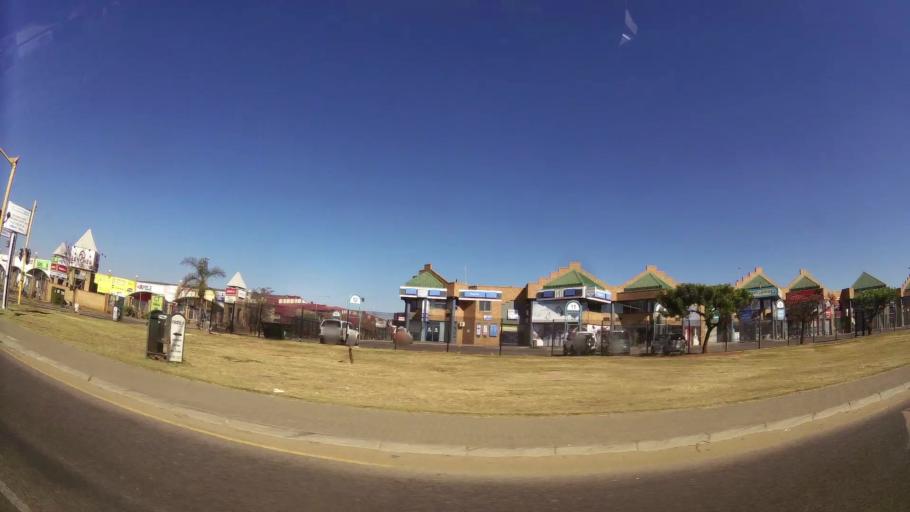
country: ZA
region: Gauteng
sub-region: City of Tshwane Metropolitan Municipality
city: Centurion
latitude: -25.8726
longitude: 28.1647
